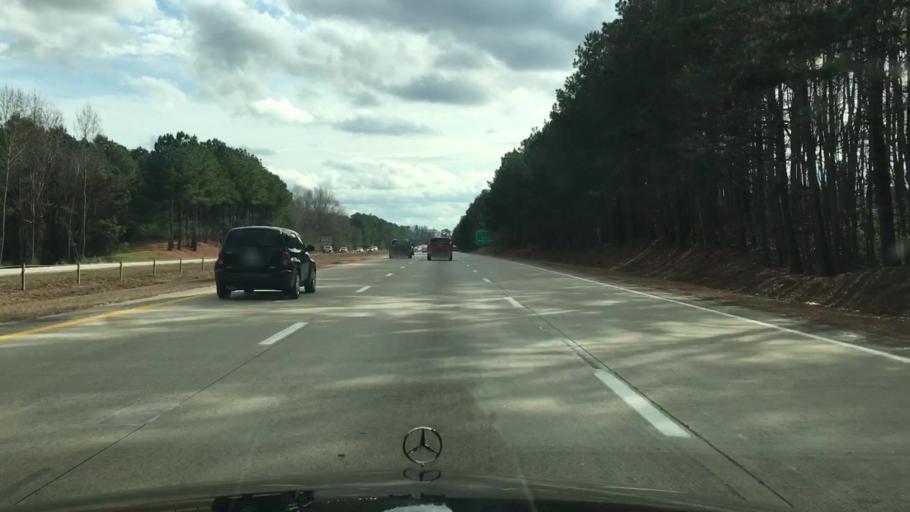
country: US
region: North Carolina
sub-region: Johnston County
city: Benson
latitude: 35.4195
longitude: -78.5286
